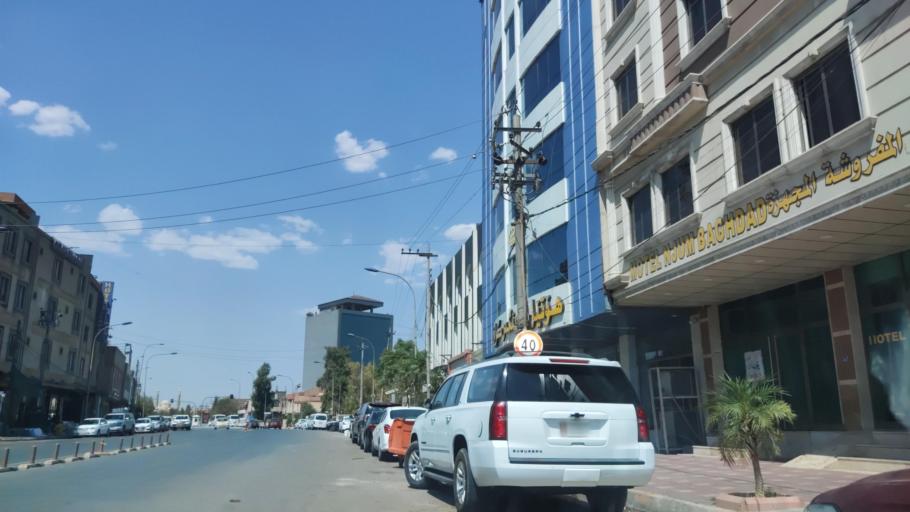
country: IQ
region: Arbil
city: Erbil
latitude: 36.1885
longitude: 44.0194
